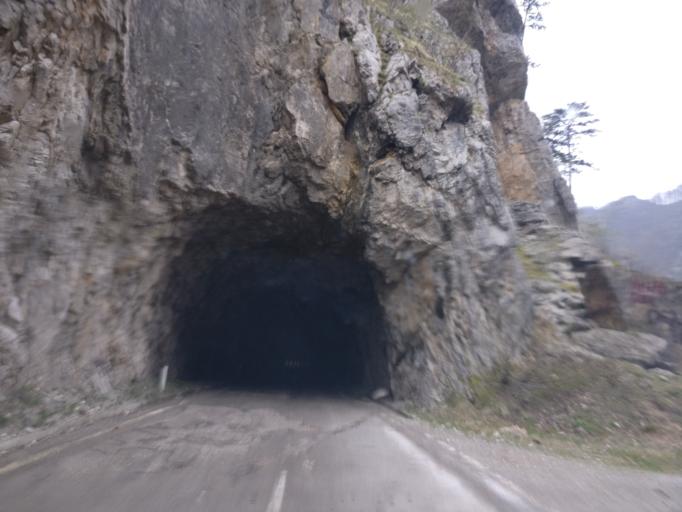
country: ME
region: Opstina Pluzine
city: Pluzine
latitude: 43.2701
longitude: 18.8414
